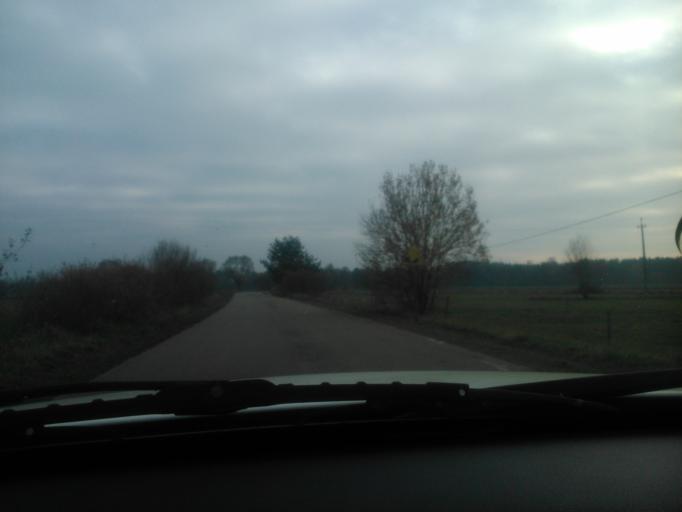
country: PL
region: Masovian Voivodeship
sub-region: Powiat ostrolecki
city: Czarnia
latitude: 53.3643
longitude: 21.1947
